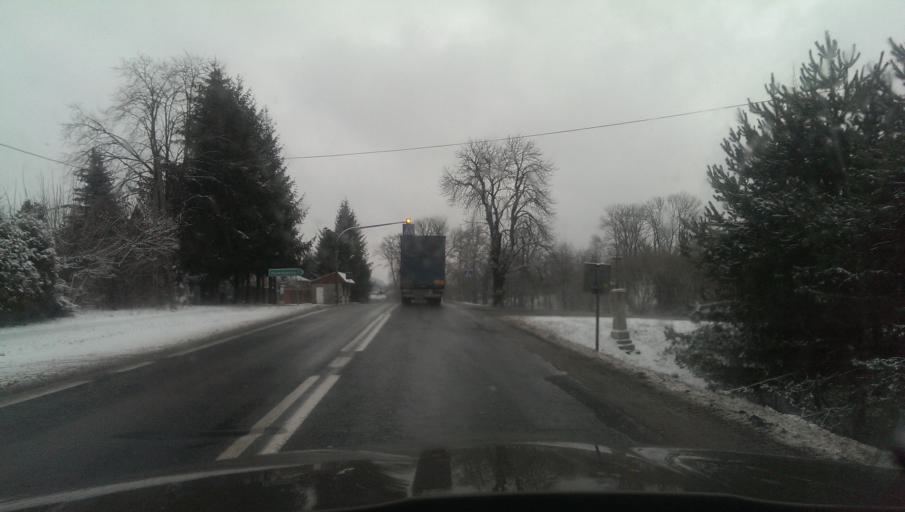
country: PL
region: Subcarpathian Voivodeship
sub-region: Powiat sanocki
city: Nowosielce-Gniewosz
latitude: 49.5583
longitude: 22.0954
